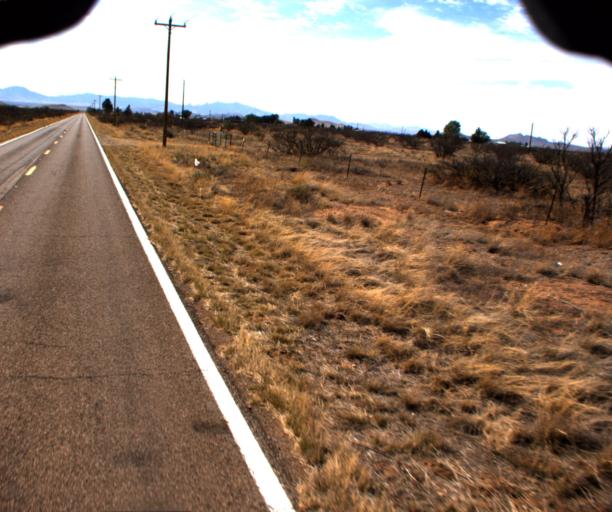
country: US
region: Arizona
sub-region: Cochise County
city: Willcox
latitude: 31.8762
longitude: -109.6154
